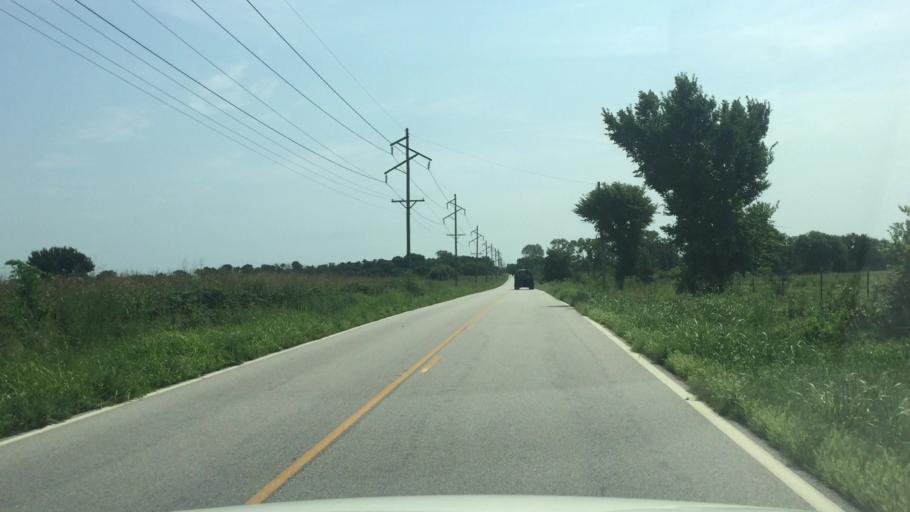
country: US
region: Kansas
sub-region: Montgomery County
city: Cherryvale
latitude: 37.2084
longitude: -95.5722
